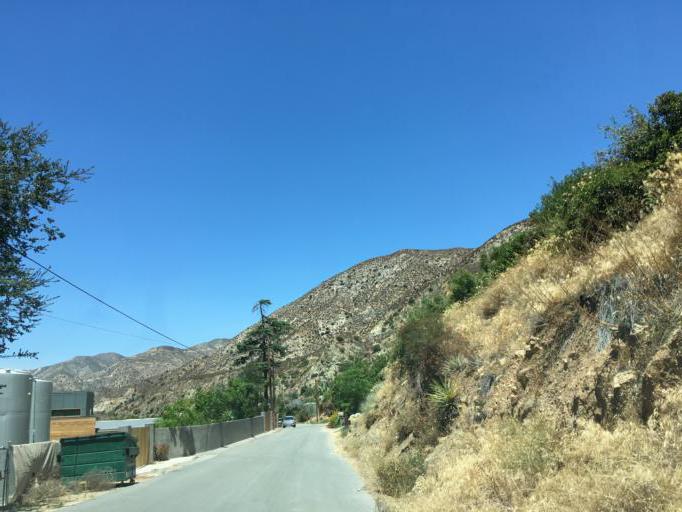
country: US
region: California
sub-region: Los Angeles County
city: La Crescenta-Montrose
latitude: 34.2888
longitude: -118.2317
